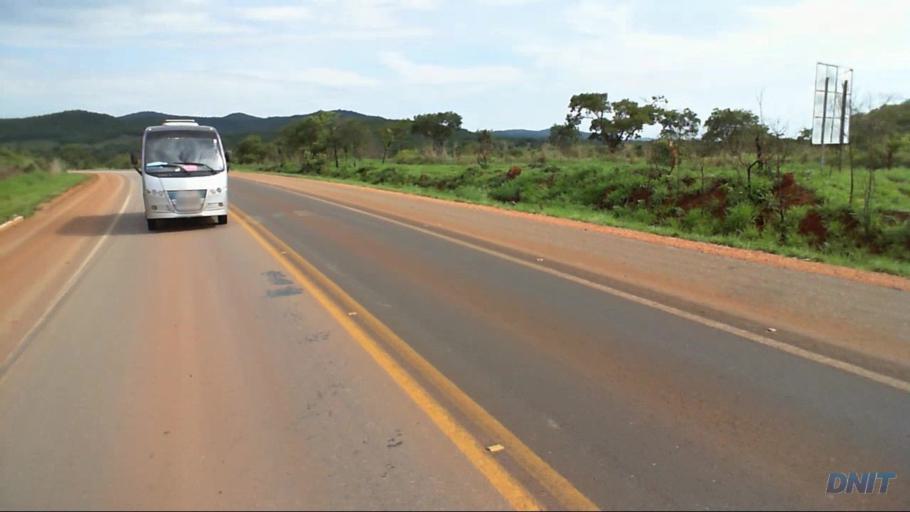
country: BR
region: Goias
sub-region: Barro Alto
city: Barro Alto
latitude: -14.9514
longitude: -48.9326
